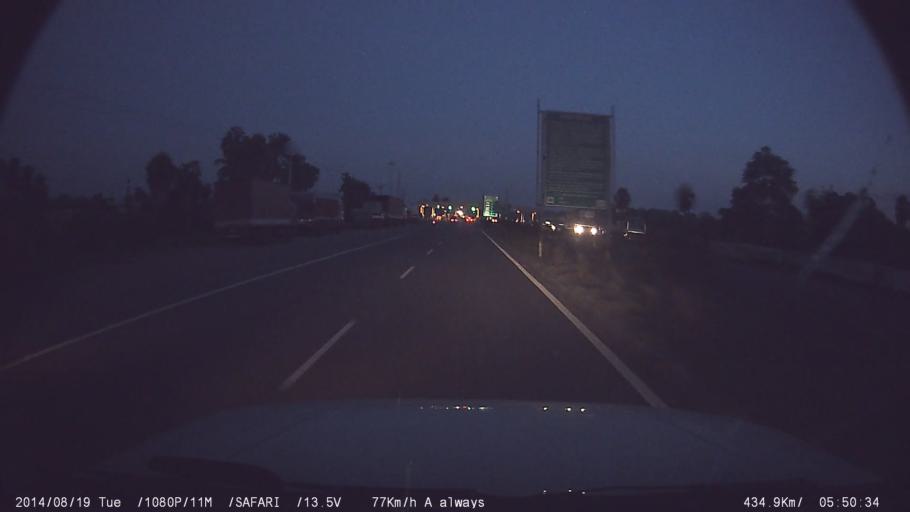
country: IN
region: Tamil Nadu
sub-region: Salem
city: Omalur
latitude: 11.7178
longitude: 78.0758
